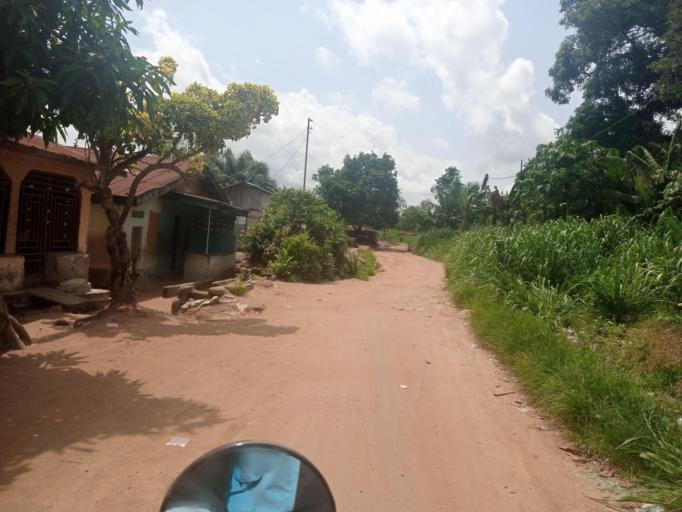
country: SL
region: Southern Province
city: Bo
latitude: 7.9623
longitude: -11.7516
